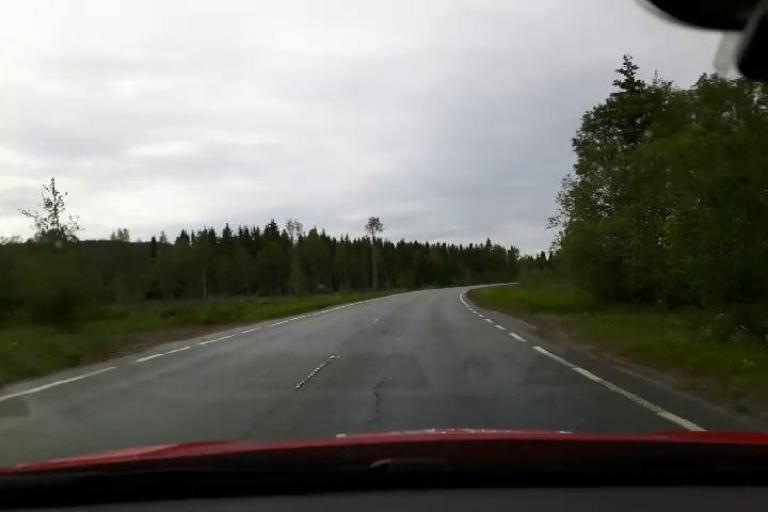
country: SE
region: Jaemtland
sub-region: Bergs Kommun
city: Hoverberg
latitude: 62.9066
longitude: 14.3330
